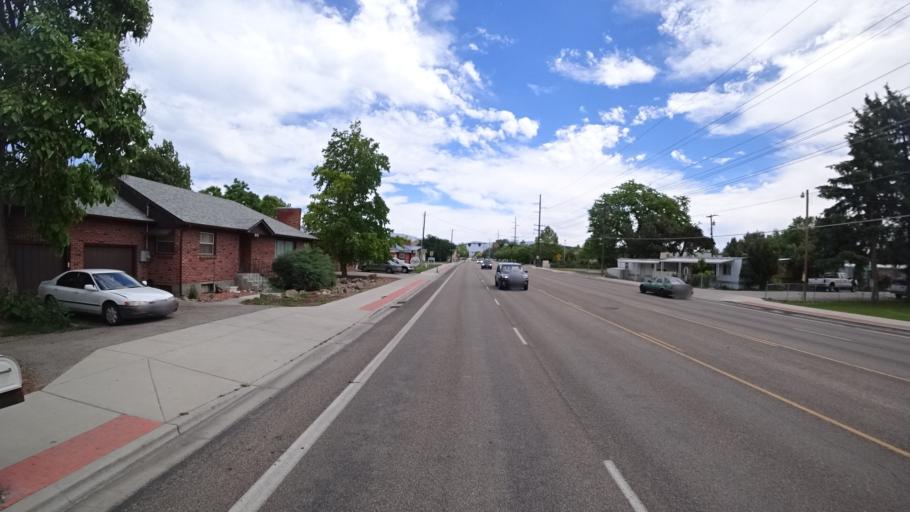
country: US
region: Idaho
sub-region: Ada County
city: Garden City
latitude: 43.6340
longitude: -116.2779
